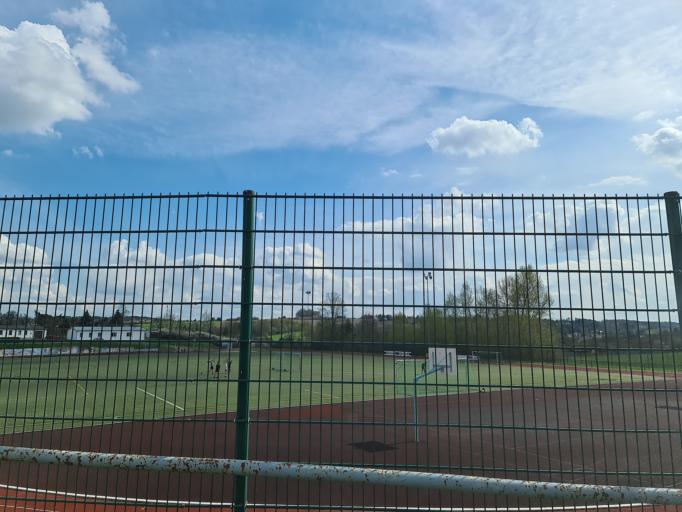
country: DE
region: Saxony
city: Plauen
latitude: 50.4903
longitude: 12.1152
